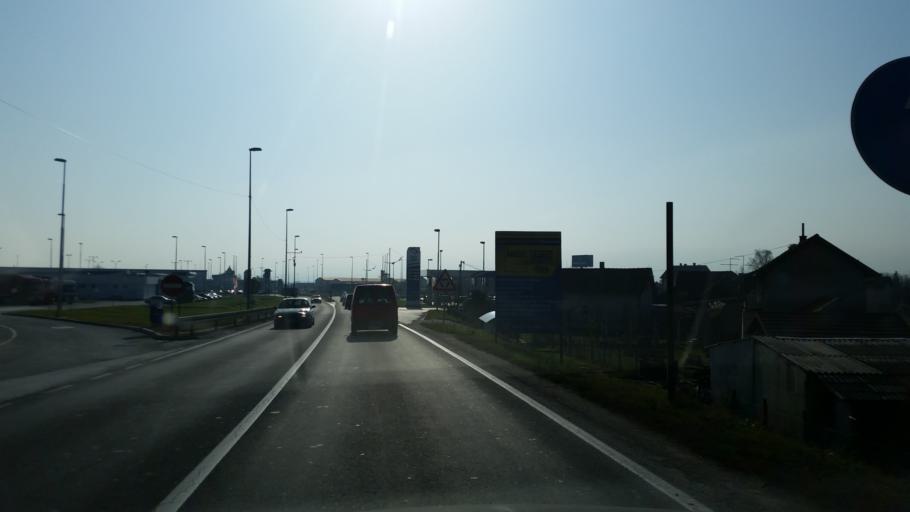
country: RS
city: Prislonica
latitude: 43.9147
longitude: 20.4075
